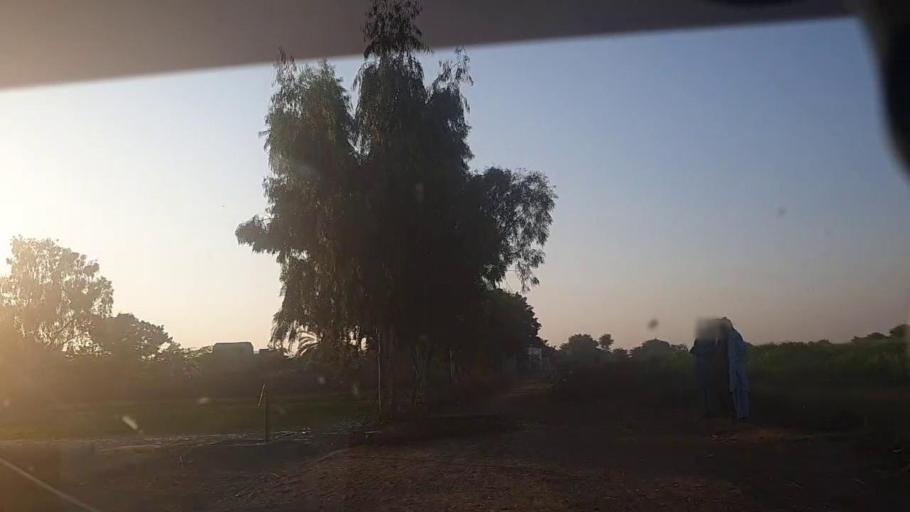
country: PK
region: Sindh
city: Sobhadero
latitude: 27.3625
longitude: 68.4133
